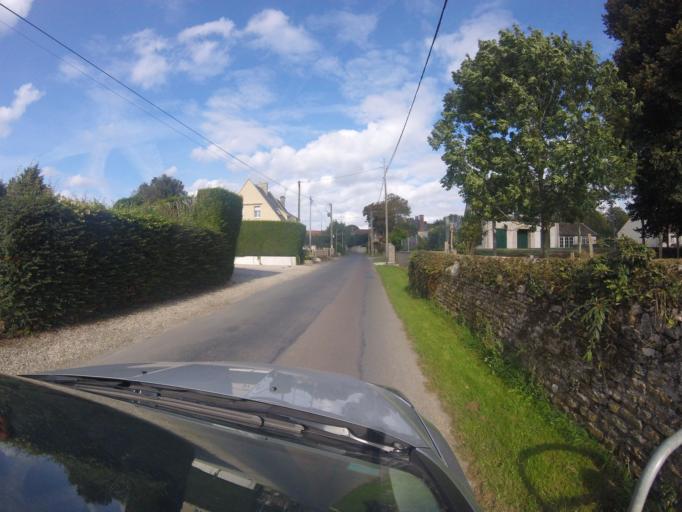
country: FR
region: Lower Normandy
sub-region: Departement du Calvados
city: Saint-Vigor-le-Grand
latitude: 49.3386
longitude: -0.6932
